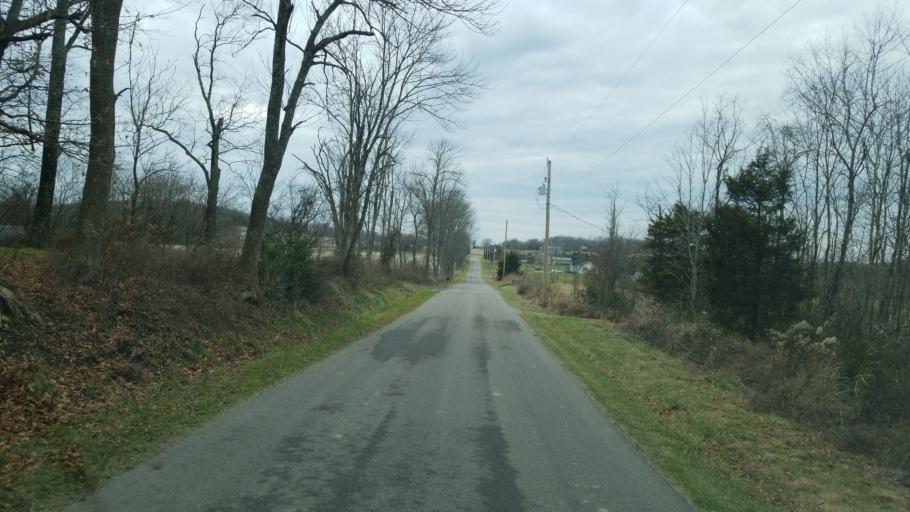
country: US
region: Ohio
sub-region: Highland County
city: Greenfield
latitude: 39.2995
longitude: -83.3518
